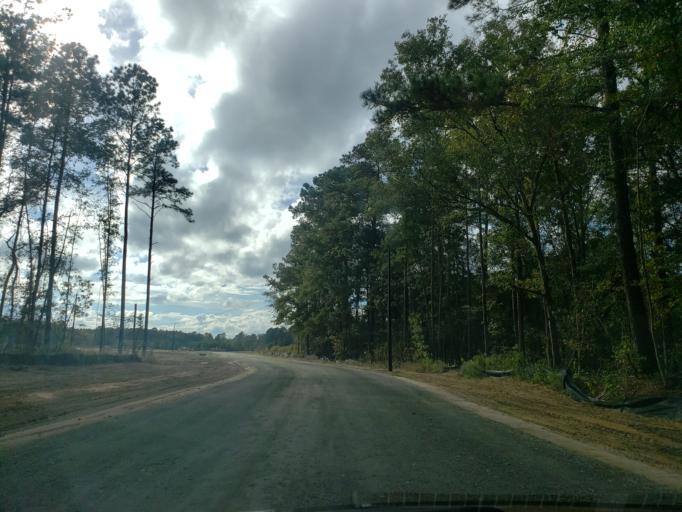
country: US
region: Georgia
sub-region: Chatham County
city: Georgetown
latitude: 32.0074
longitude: -81.2915
